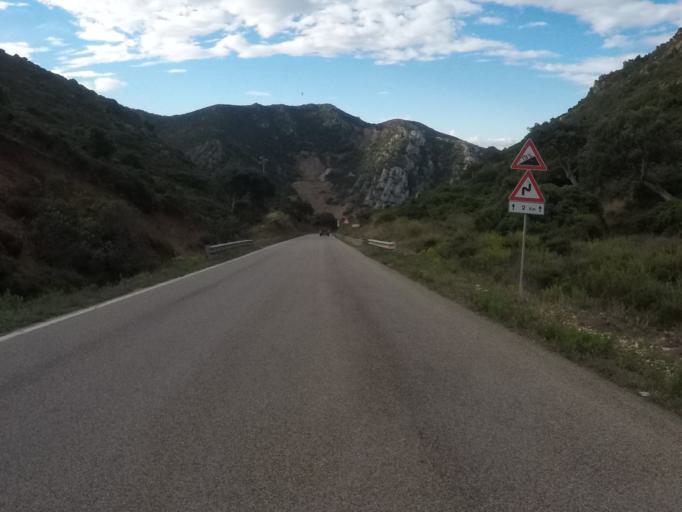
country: IT
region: Sardinia
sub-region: Provincia di Carbonia-Iglesias
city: Buggerru
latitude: 39.3389
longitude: 8.4400
